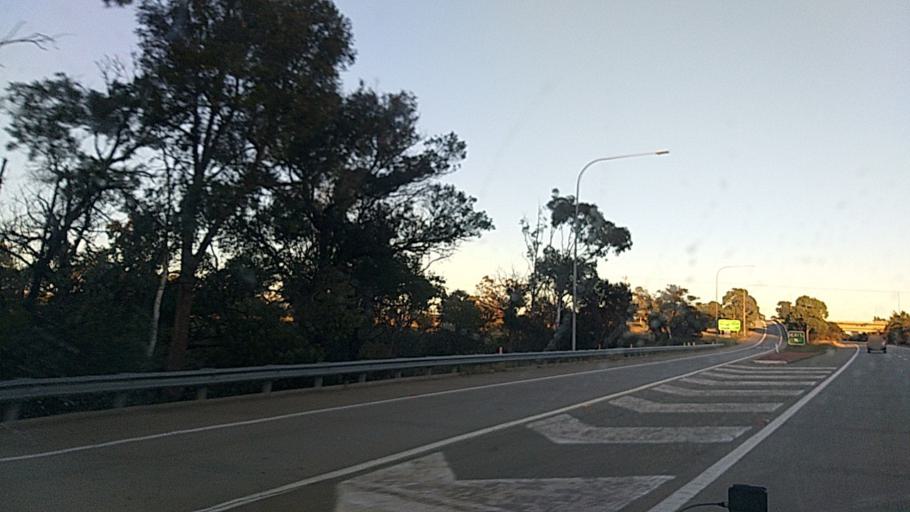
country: AU
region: New South Wales
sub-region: Goulburn Mulwaree
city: Goulburn
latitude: -34.7761
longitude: 149.6921
